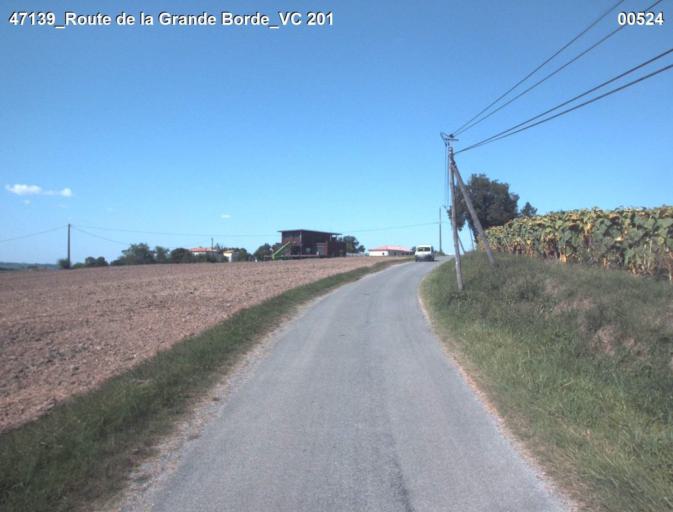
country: FR
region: Aquitaine
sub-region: Departement du Lot-et-Garonne
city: Nerac
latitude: 44.0669
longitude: 0.3926
